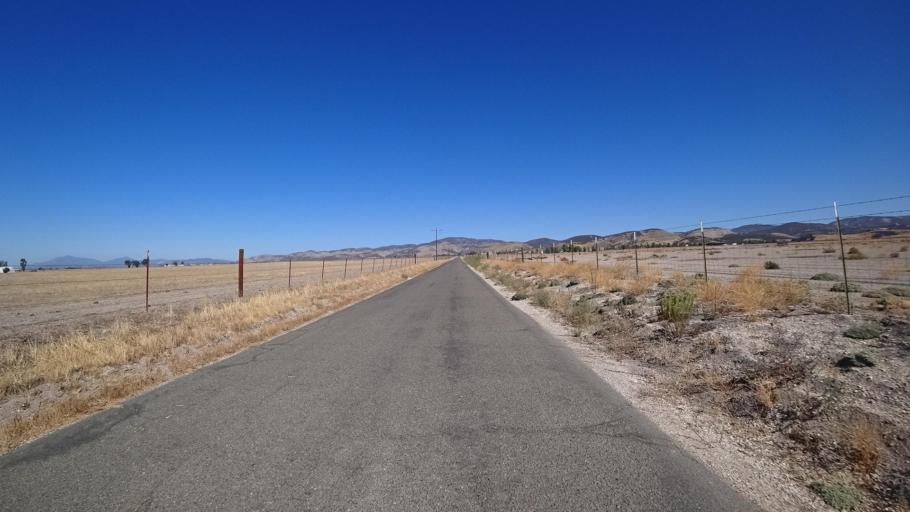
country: US
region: California
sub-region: Monterey County
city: King City
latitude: 35.9452
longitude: -121.0828
